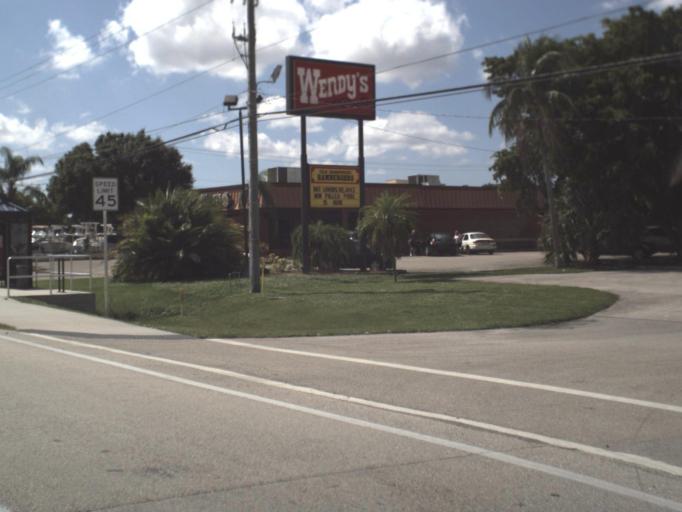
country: US
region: Florida
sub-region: Lee County
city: Pine Manor
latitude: 26.5670
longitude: -81.8721
